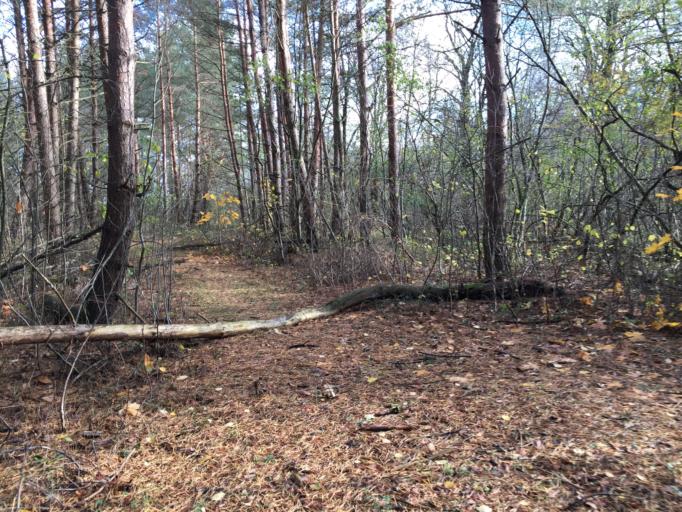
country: LV
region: Carnikava
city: Carnikava
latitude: 57.1539
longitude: 24.2571
